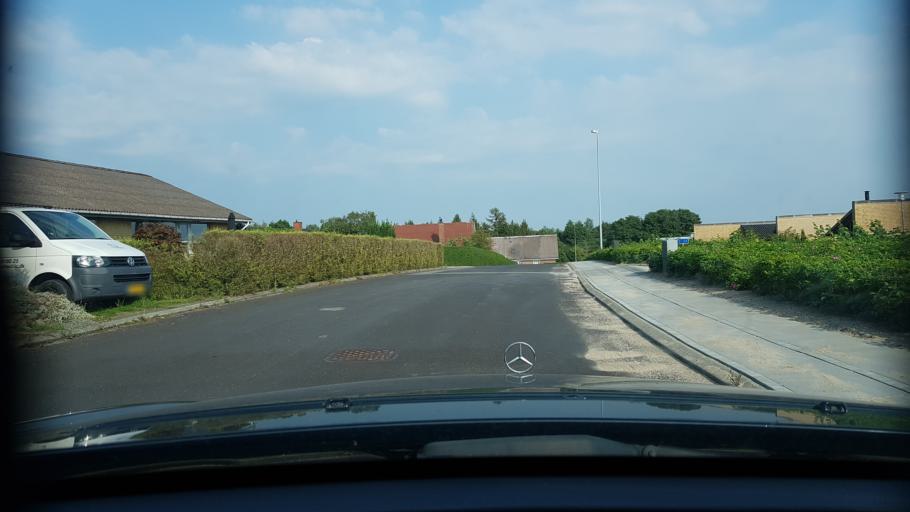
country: DK
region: North Denmark
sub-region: Mariagerfjord Kommune
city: Hadsund
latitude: 56.7244
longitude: 10.1183
